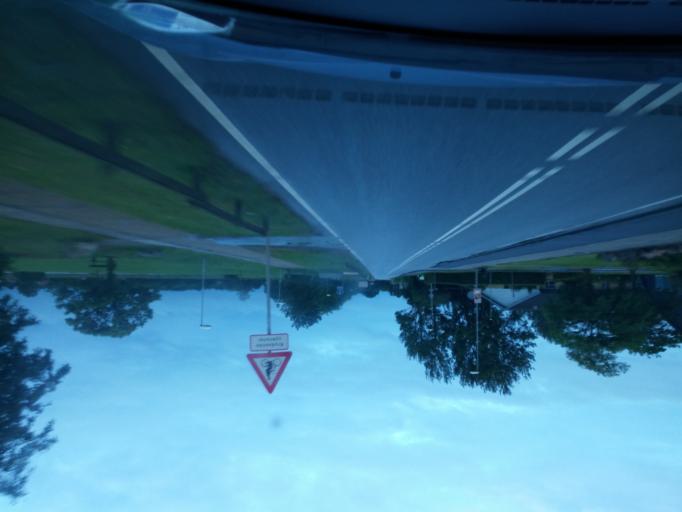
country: DK
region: South Denmark
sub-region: Kerteminde Kommune
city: Kerteminde
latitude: 55.4453
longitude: 10.6582
